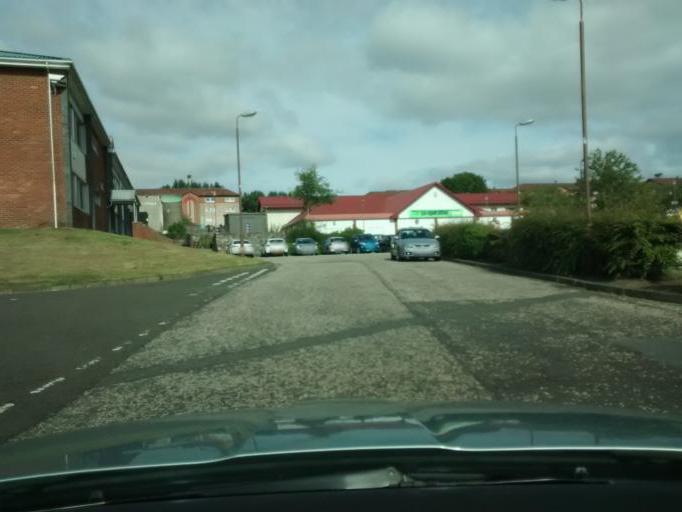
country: GB
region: Scotland
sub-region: West Lothian
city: Mid Calder
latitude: 55.8963
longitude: -3.4965
